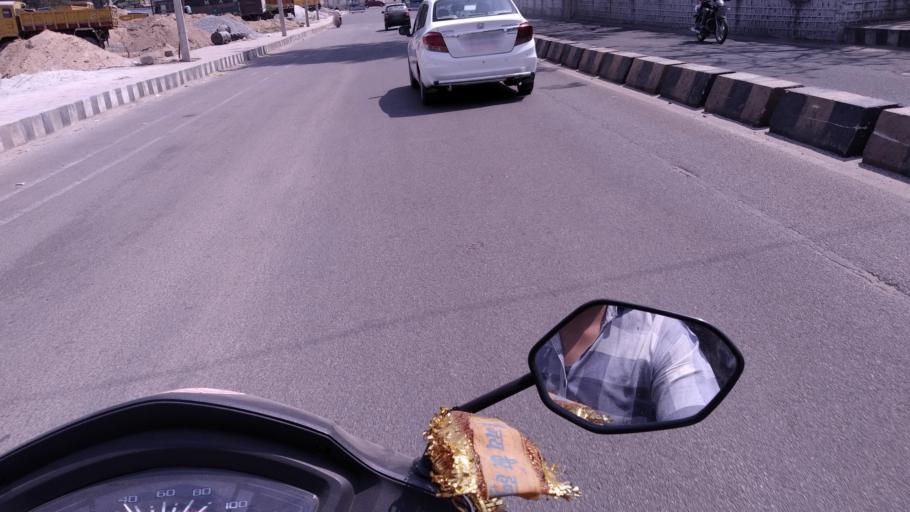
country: IN
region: Telangana
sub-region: Hyderabad
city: Malkajgiri
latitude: 17.4513
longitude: 78.4871
